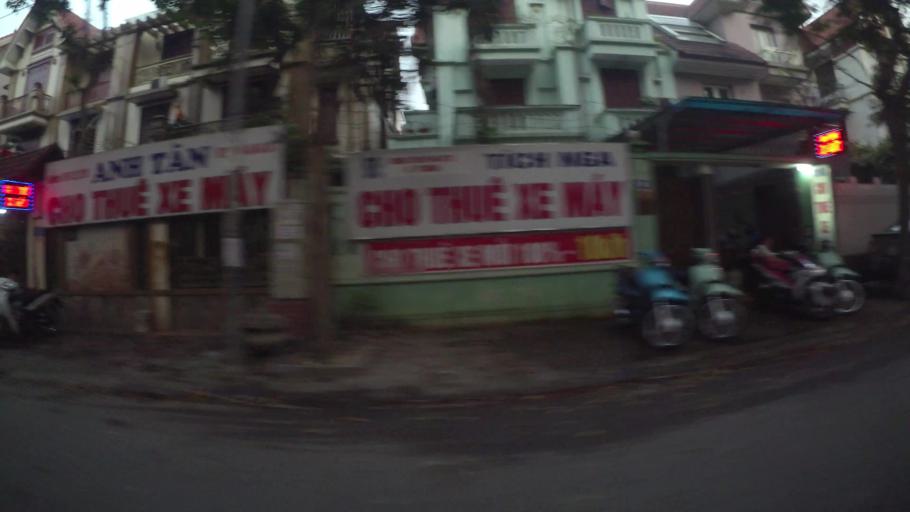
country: VN
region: Ha Noi
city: Ha Dong
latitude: 20.9786
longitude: 105.7928
